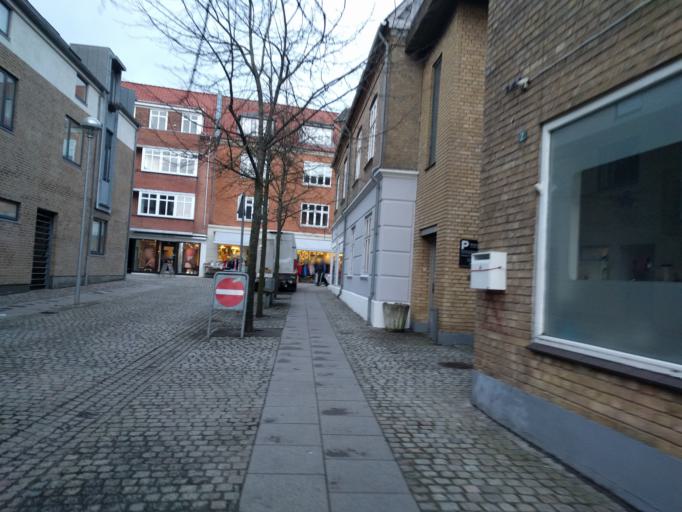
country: DK
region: North Denmark
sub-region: Alborg Kommune
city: Aalborg
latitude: 57.0590
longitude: 9.9208
